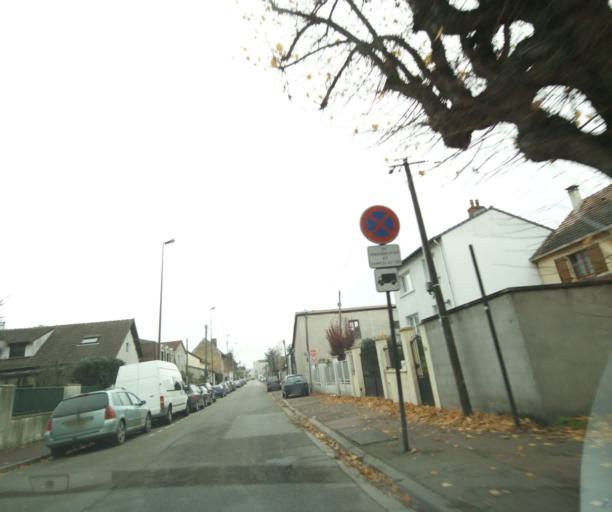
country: FR
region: Ile-de-France
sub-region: Departement de Seine-Saint-Denis
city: Livry-Gargan
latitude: 48.9182
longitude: 2.5287
